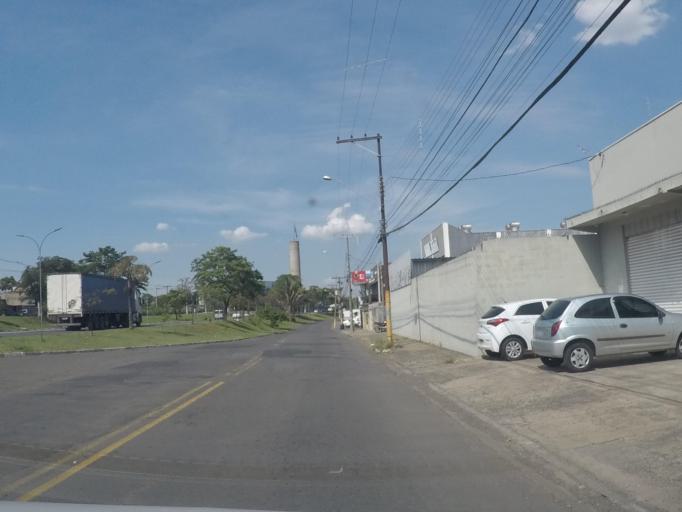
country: BR
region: Sao Paulo
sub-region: Sumare
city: Sumare
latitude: -22.8087
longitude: -47.2550
